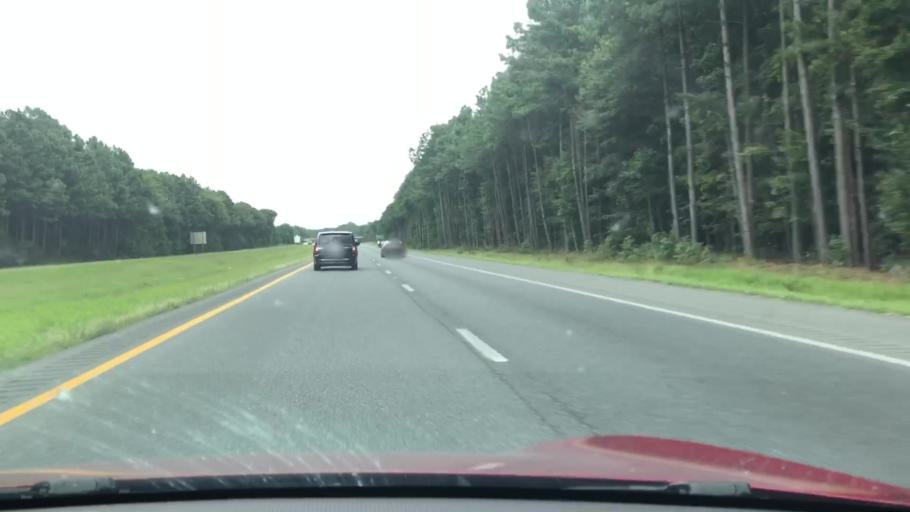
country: US
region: Maryland
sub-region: Wicomico County
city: Salisbury
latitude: 38.3378
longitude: -75.5582
